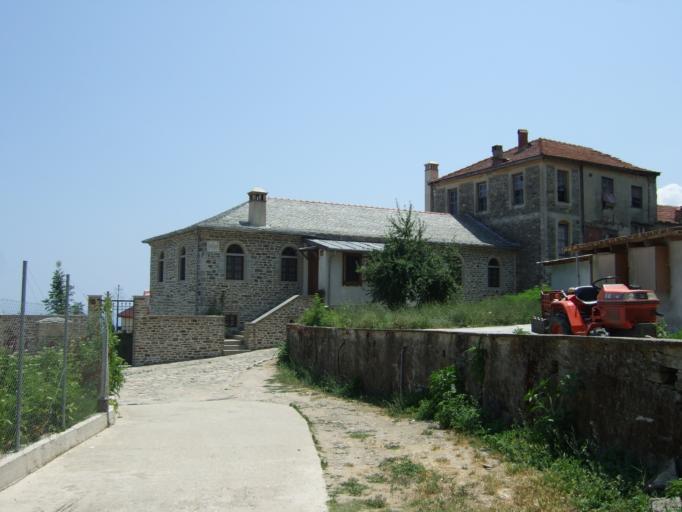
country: GR
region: Mount Athos
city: Karyes
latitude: 40.2574
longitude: 24.2463
